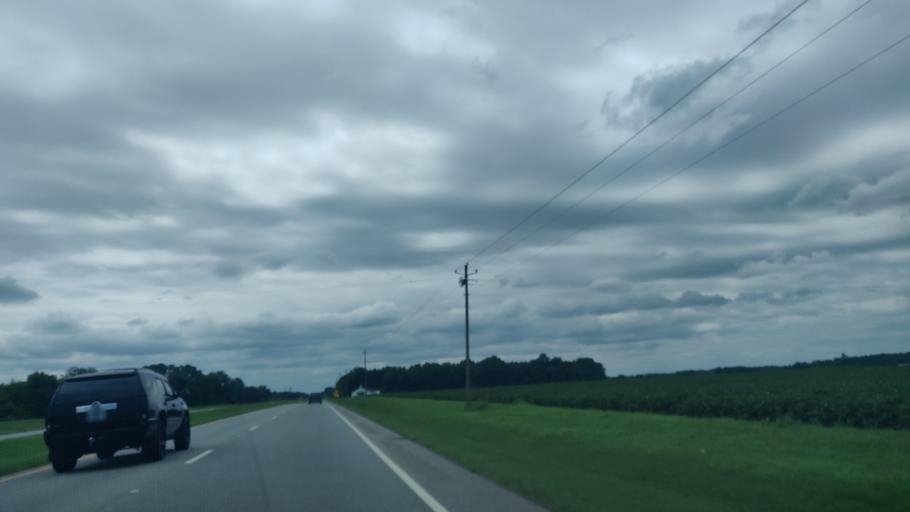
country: US
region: Georgia
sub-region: Terrell County
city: Dawson
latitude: 31.8233
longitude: -84.4607
